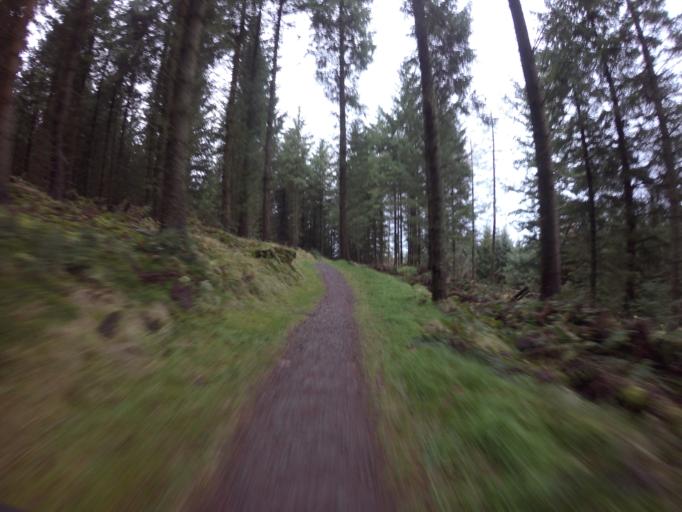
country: GB
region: Scotland
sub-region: The Scottish Borders
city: Peebles
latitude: 55.6582
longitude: -3.1613
